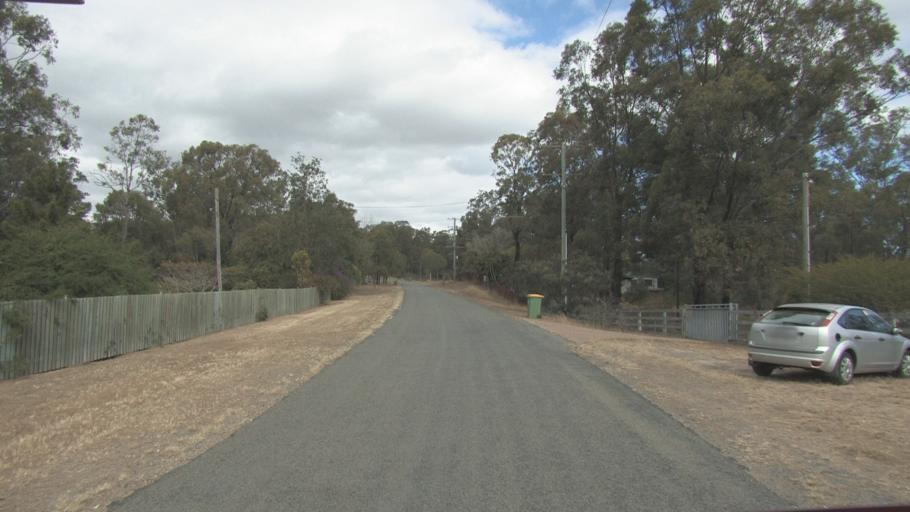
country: AU
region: Queensland
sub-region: Logan
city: Cedar Vale
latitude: -27.8888
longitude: 153.0235
